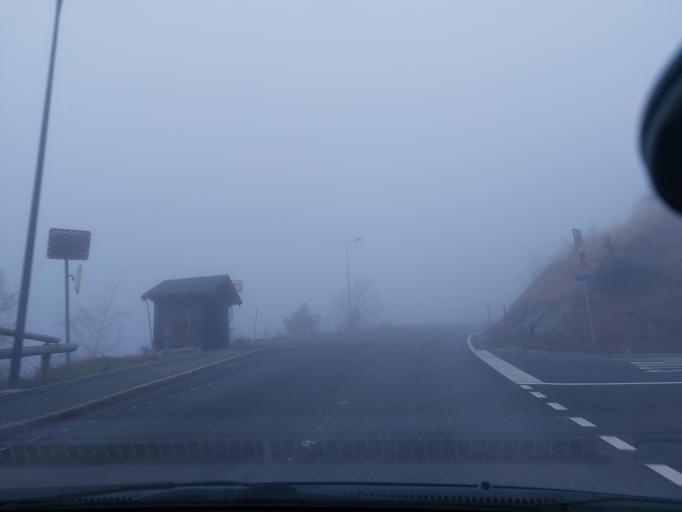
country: CH
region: Valais
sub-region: Sierre District
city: Lens
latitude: 46.2944
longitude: 7.4496
